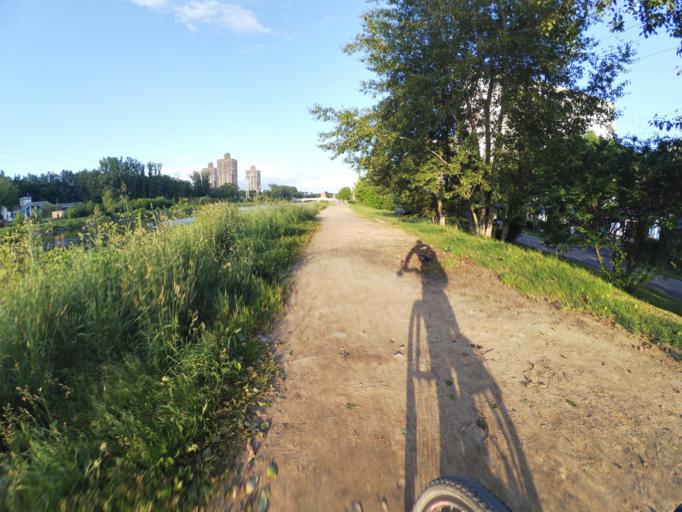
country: RU
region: Moscow
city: Pokrovskoye-Streshnevo
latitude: 55.8355
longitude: 37.4470
